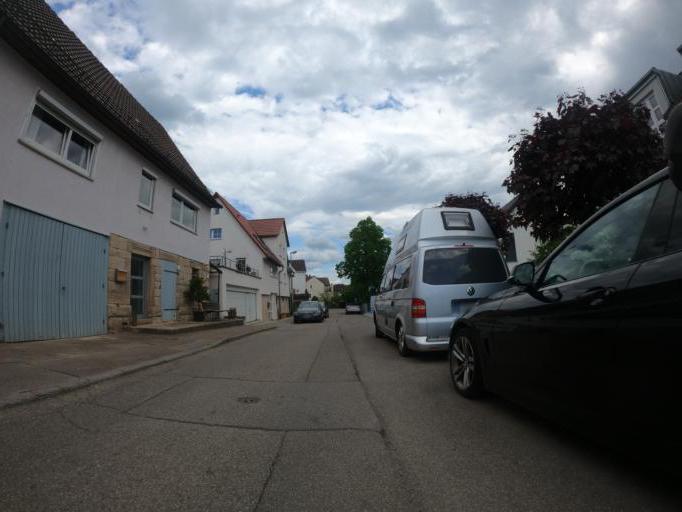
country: DE
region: Baden-Wuerttemberg
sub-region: Tuebingen Region
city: Dettenhausen
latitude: 48.6090
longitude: 9.0951
